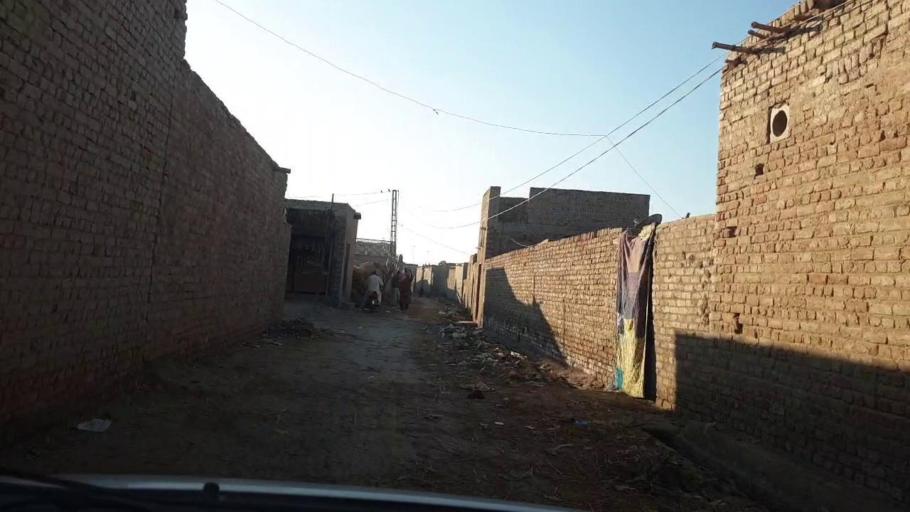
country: PK
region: Sindh
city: Khairpur Nathan Shah
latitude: 27.0709
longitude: 67.7258
